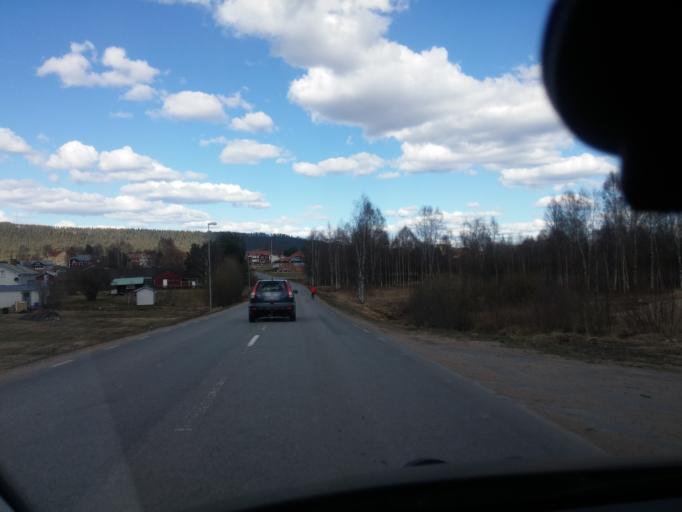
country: SE
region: Gaevleborg
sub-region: Ljusdals Kommun
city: Farila
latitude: 61.7943
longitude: 15.8341
